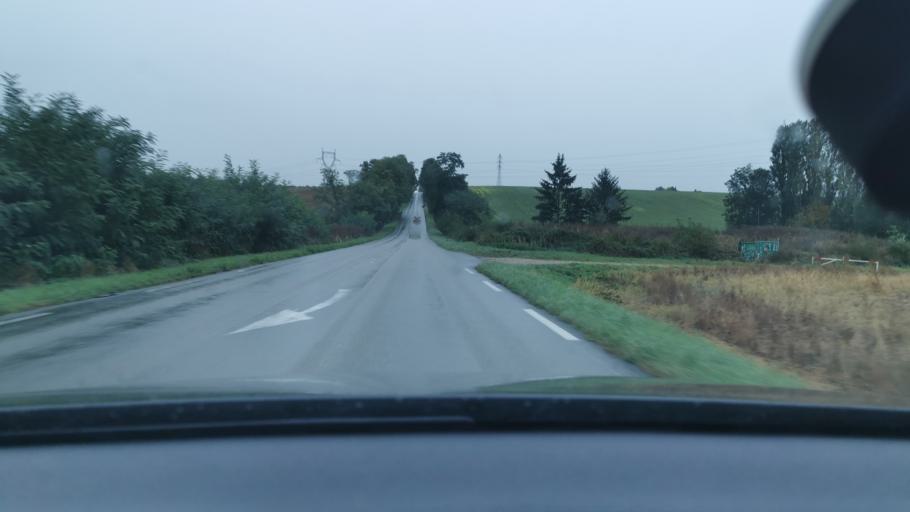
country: FR
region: Rhone-Alpes
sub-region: Departement du Rhone
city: Montanay
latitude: 45.8865
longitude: 4.8828
